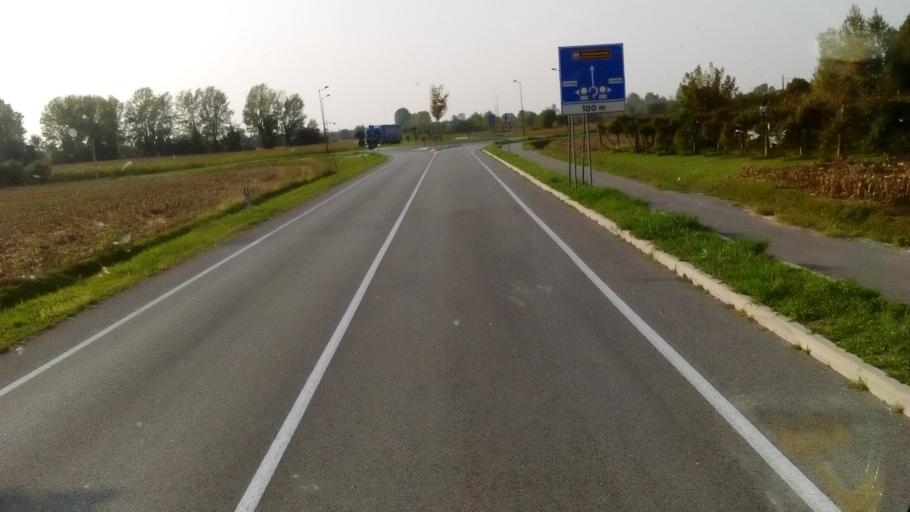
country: IT
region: Veneto
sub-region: Provincia di Padova
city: Mejaniga
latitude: 45.4706
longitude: 11.9161
